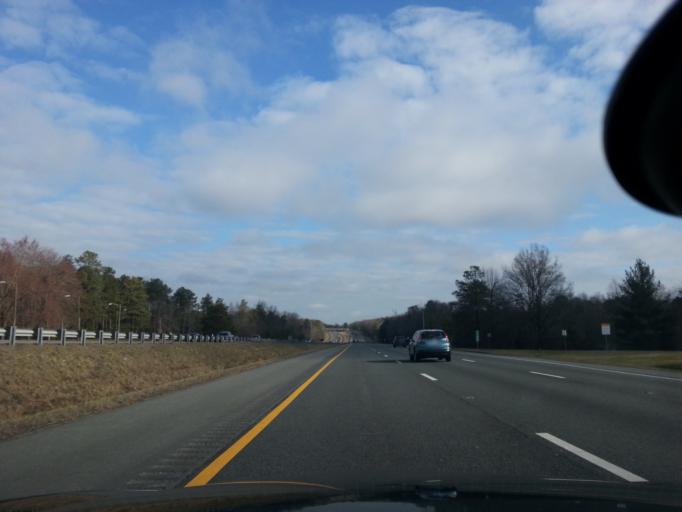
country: US
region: Virginia
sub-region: Caroline County
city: Bowling Green
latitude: 37.9814
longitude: -77.4926
